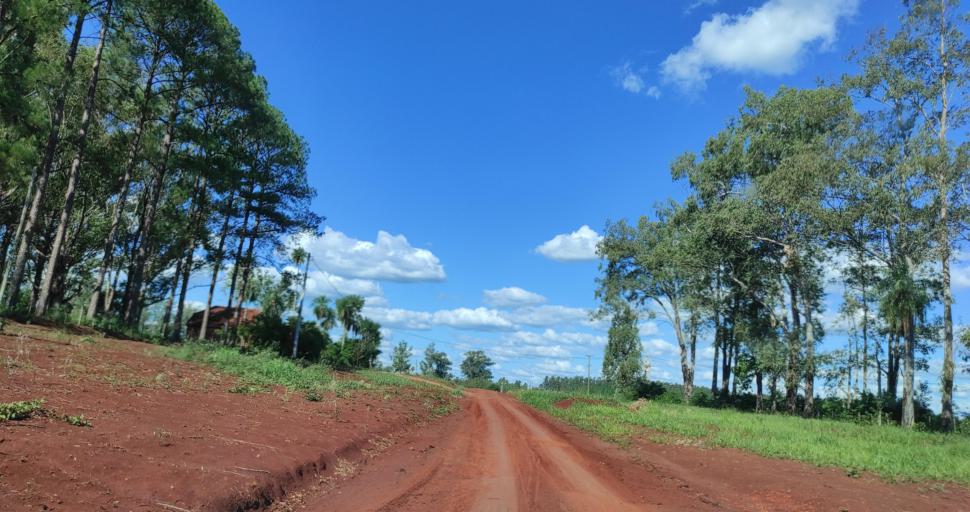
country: AR
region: Misiones
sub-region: Departamento de Candelaria
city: Candelaria
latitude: -27.4649
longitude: -55.7133
